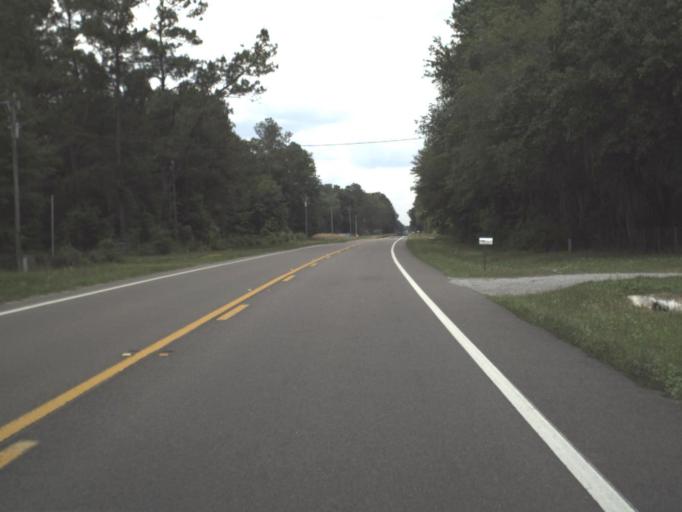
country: US
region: Florida
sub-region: Columbia County
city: Five Points
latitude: 30.3234
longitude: -82.6295
